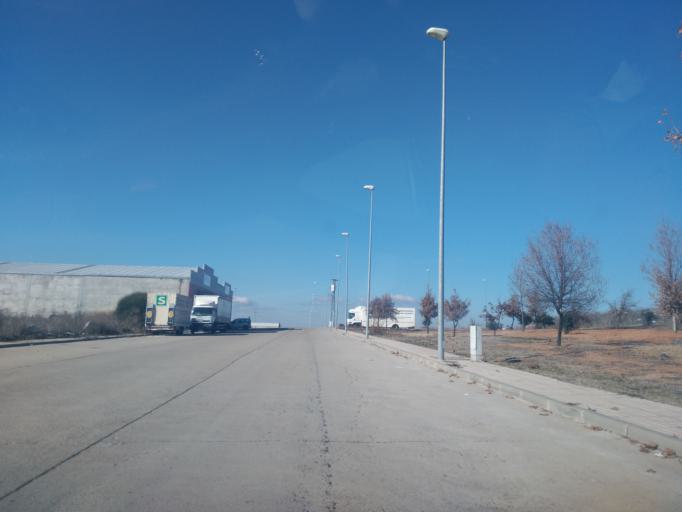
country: ES
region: Castille and Leon
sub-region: Provincia de Salamanca
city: Villares de la Reina
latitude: 40.9953
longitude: -5.6453
